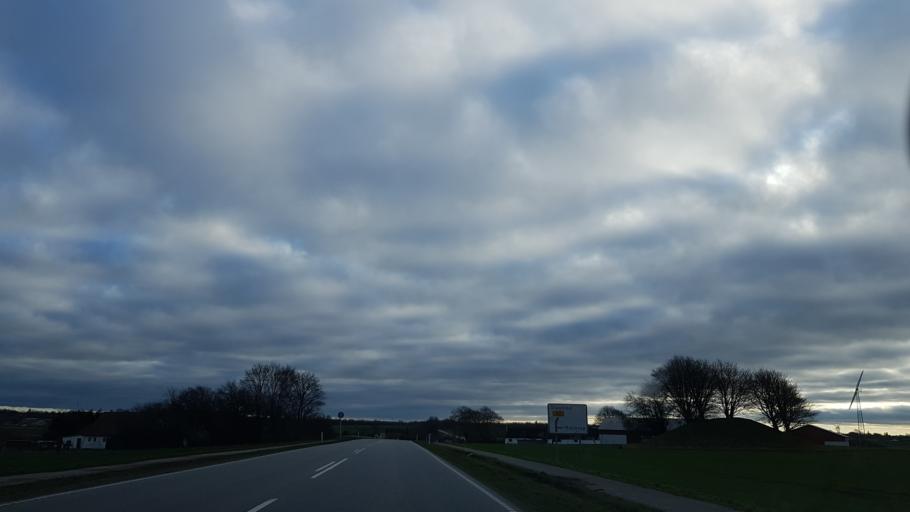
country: DK
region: Zealand
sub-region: Kalundborg Kommune
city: Hong
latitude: 55.5070
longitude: 11.2597
